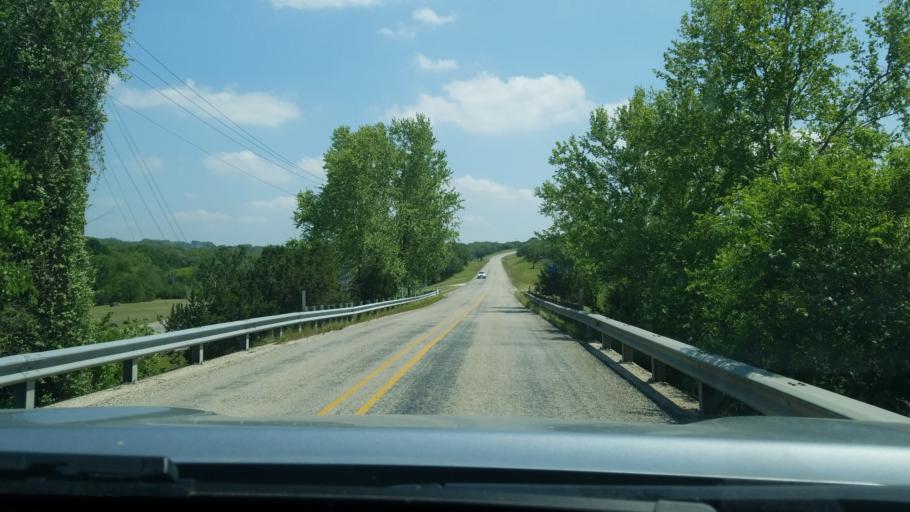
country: US
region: Texas
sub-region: Bexar County
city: Fair Oaks Ranch
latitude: 29.8921
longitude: -98.5589
